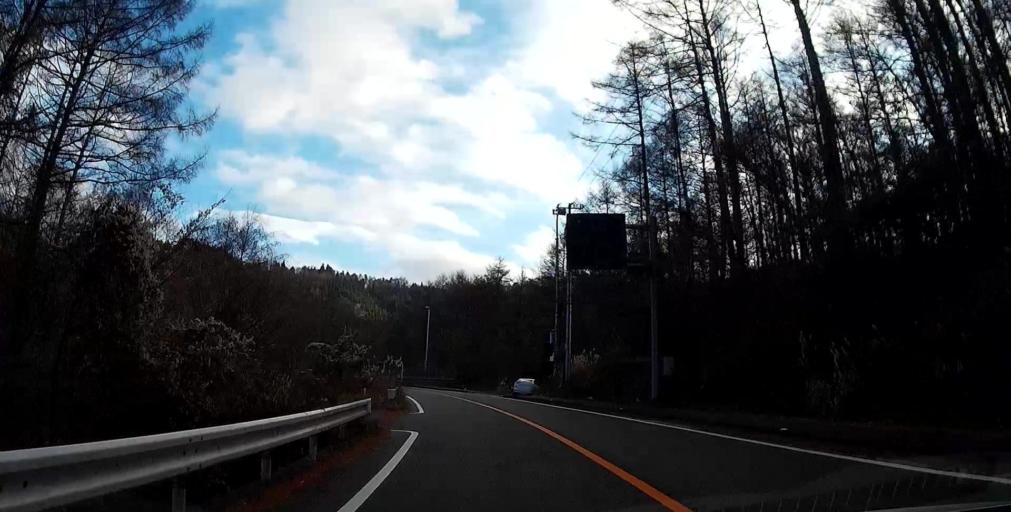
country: JP
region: Yamanashi
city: Fujikawaguchiko
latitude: 35.4759
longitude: 138.8351
